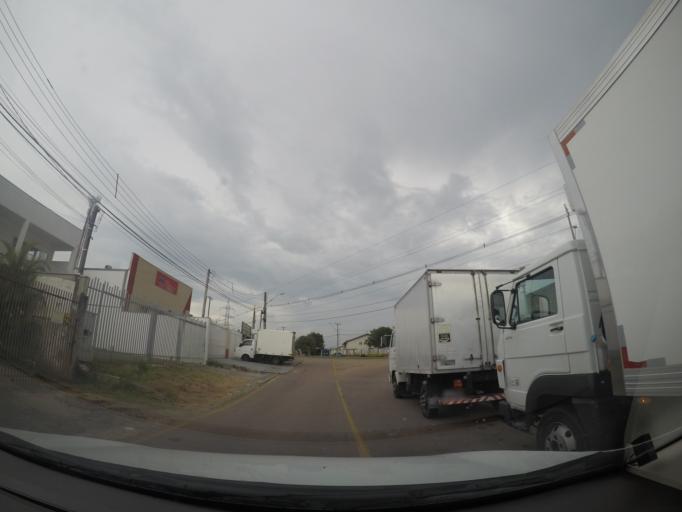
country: BR
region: Parana
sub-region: Sao Jose Dos Pinhais
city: Sao Jose dos Pinhais
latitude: -25.5386
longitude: -49.2763
